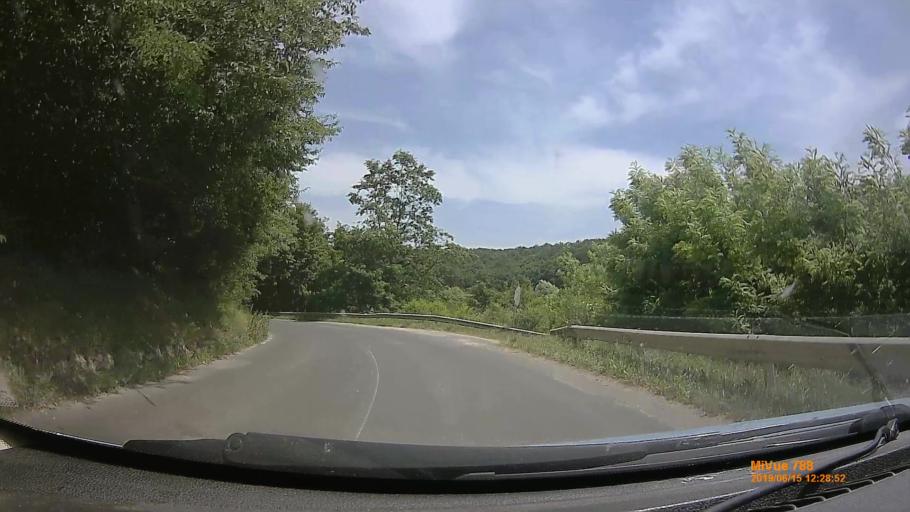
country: HU
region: Baranya
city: Buekkoesd
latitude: 46.1232
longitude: 18.0272
